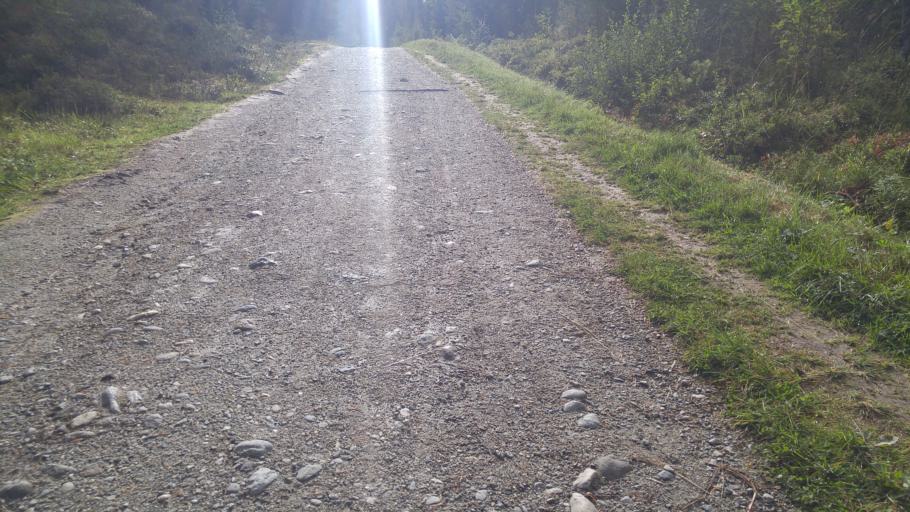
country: NO
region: Sor-Trondelag
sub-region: Trondheim
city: Trondheim
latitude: 63.4086
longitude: 10.3327
